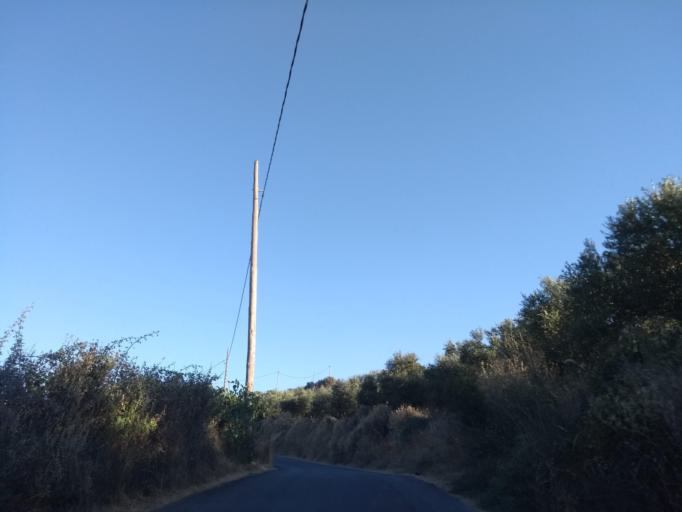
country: GR
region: Crete
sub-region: Nomos Chanias
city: Kalivai
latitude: 35.4330
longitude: 24.1756
